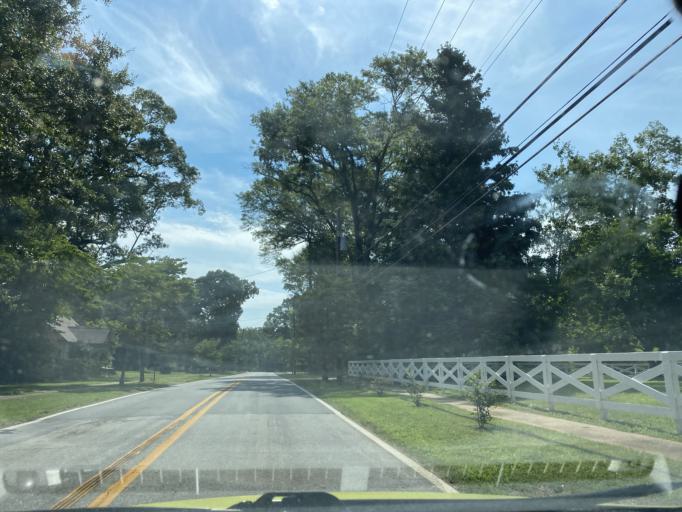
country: US
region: Georgia
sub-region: Coweta County
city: Grantville
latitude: 33.2103
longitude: -84.7429
